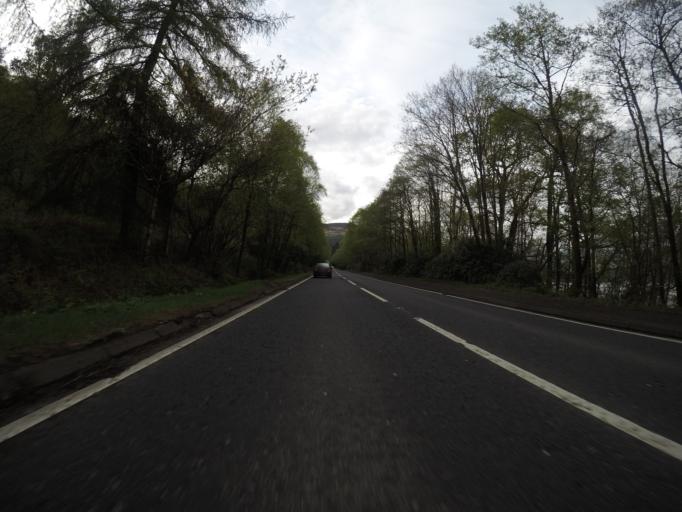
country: GB
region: Scotland
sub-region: Argyll and Bute
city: Garelochhead
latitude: 56.1977
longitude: -4.7047
